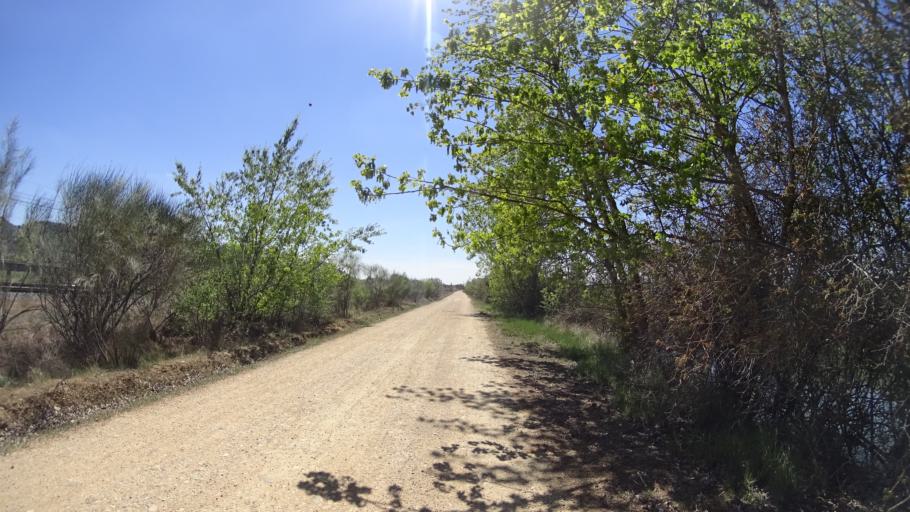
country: ES
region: Castille and Leon
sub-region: Provincia de Valladolid
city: Cabezon
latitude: 41.7577
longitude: -4.6317
